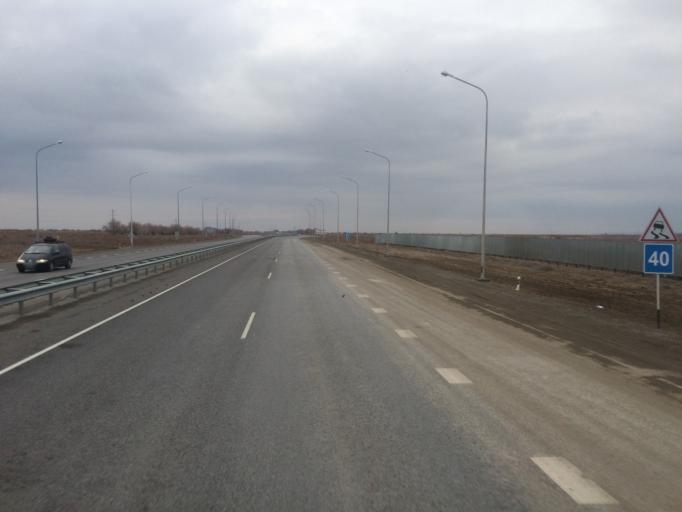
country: KZ
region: Qyzylorda
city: Shieli
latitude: 44.1406
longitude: 66.9637
